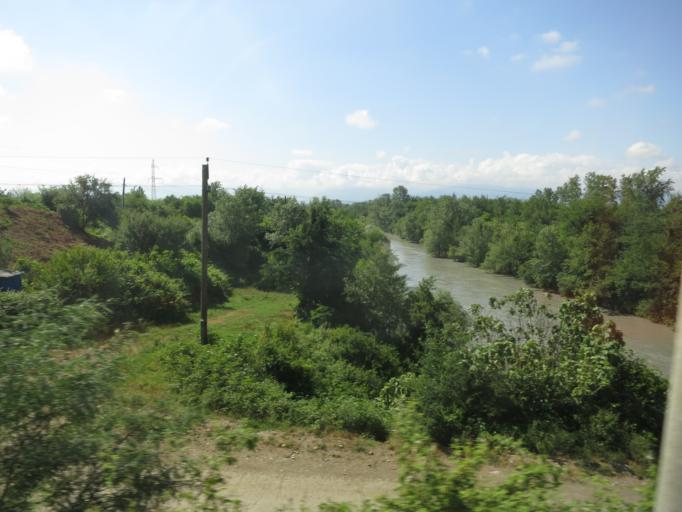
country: GE
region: Imereti
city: Kutaisi
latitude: 42.1995
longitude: 42.7269
